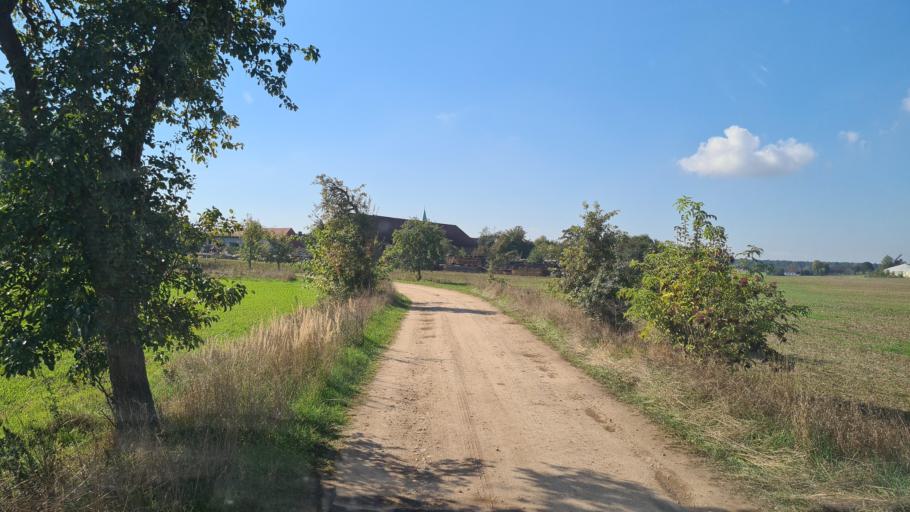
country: DE
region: Brandenburg
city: Lebusa
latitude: 51.8269
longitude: 13.4601
